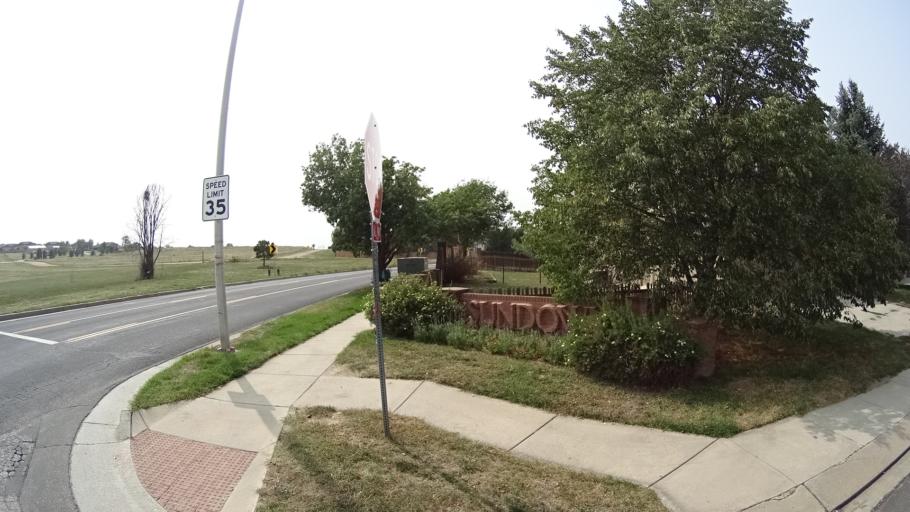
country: US
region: Colorado
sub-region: El Paso County
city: Cimarron Hills
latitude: 38.9167
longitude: -104.7286
